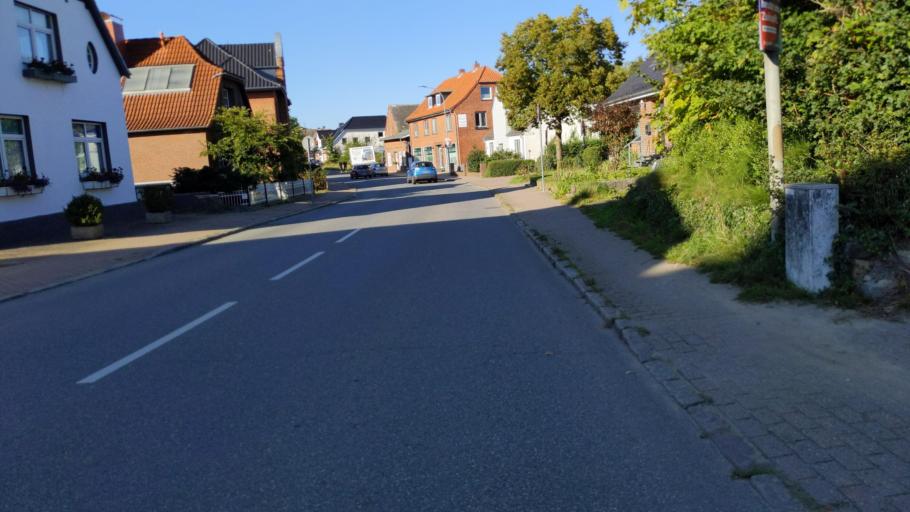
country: DE
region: Schleswig-Holstein
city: Ahrensbok
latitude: 54.0133
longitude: 10.5734
